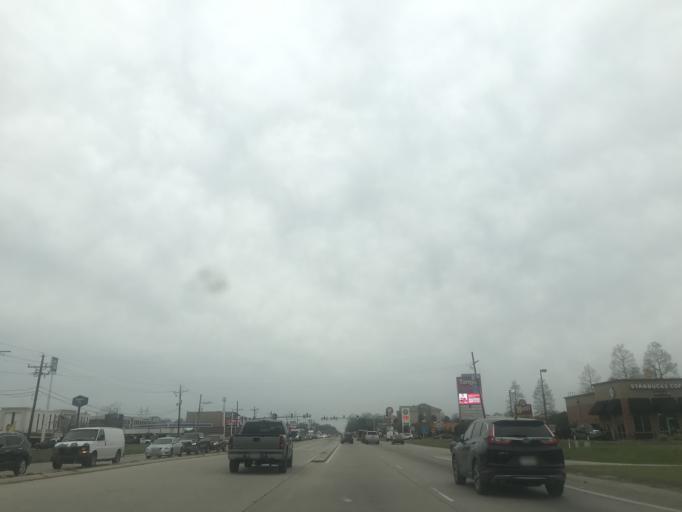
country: US
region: Louisiana
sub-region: Ascension Parish
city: Gonzales
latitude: 30.2107
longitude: -90.9490
